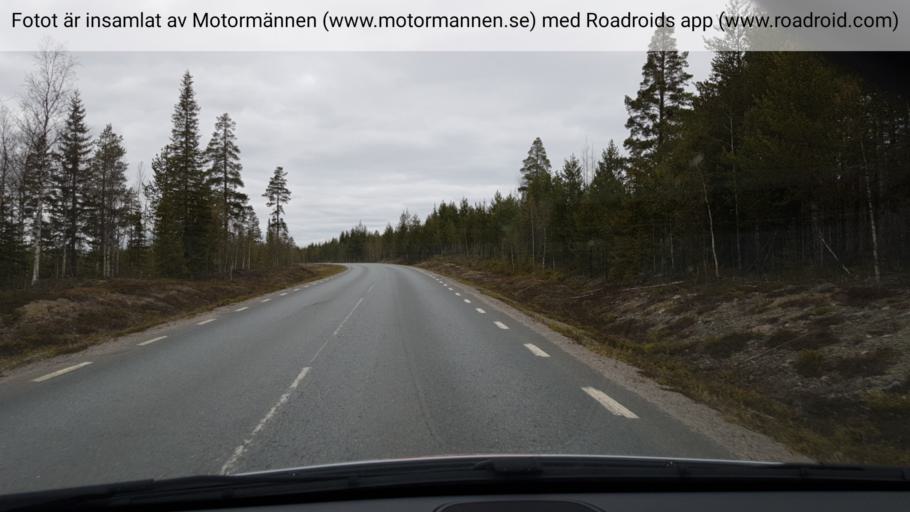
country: SE
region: Vaesterbotten
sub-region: Sorsele Kommun
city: Sorsele
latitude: 65.5091
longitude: 17.2298
